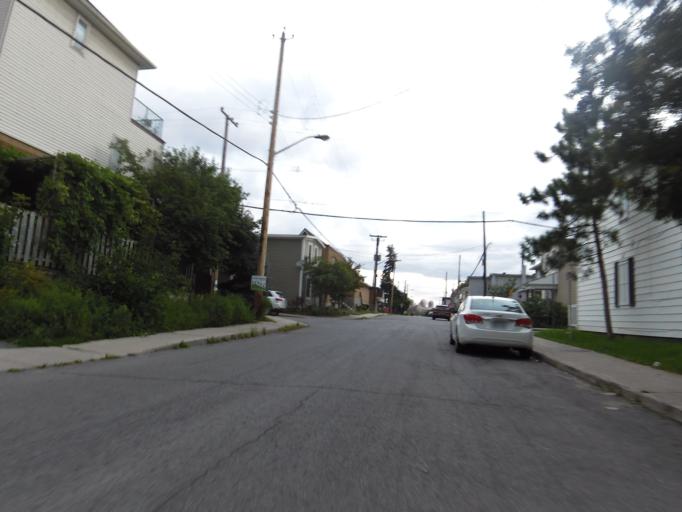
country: CA
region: Ontario
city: Ottawa
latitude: 45.4069
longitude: -75.7321
